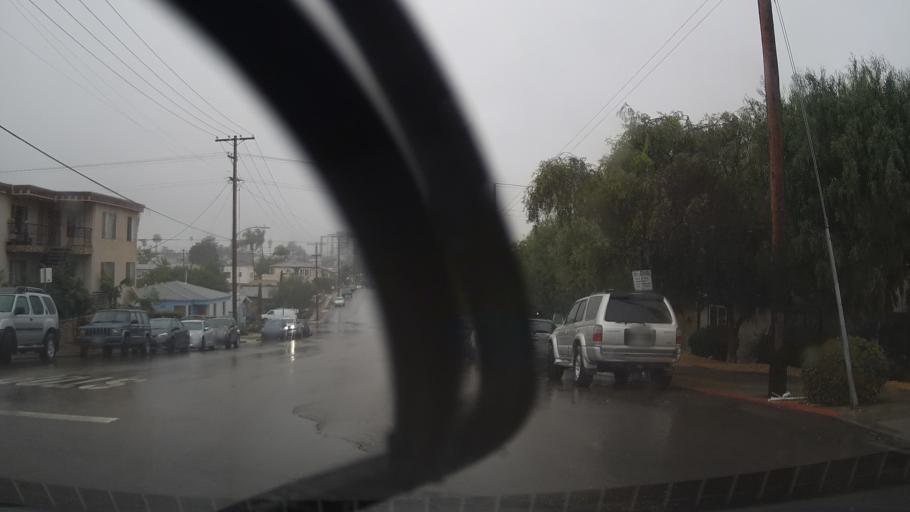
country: US
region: California
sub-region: San Diego County
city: San Diego
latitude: 32.7522
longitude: -117.1389
